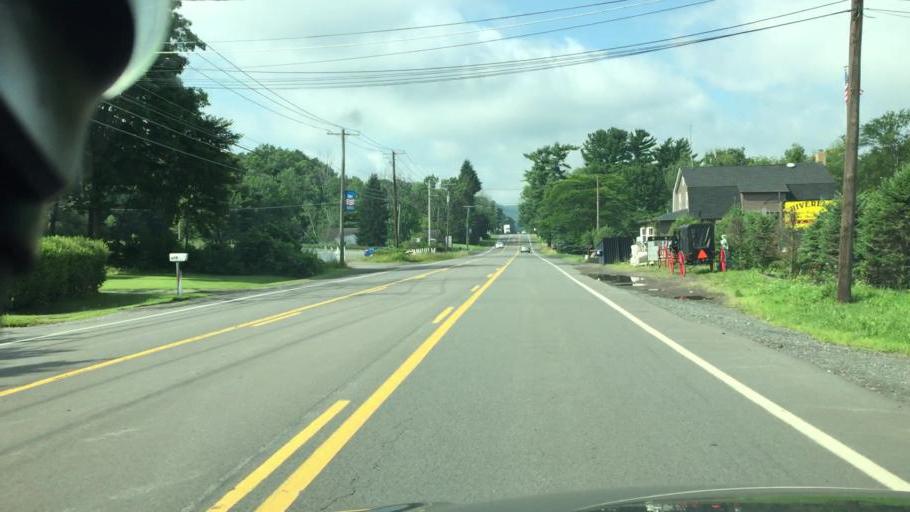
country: US
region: Pennsylvania
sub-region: Luzerne County
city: Mountain Top
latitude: 41.1139
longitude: -75.9127
